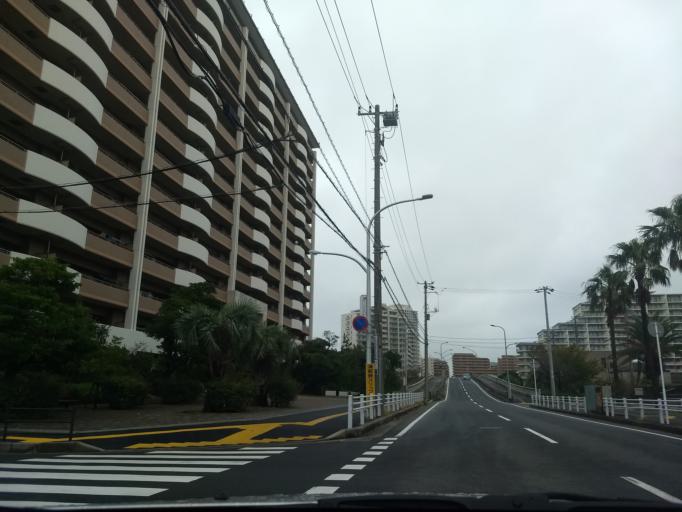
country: JP
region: Tokyo
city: Urayasu
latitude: 35.6362
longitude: 139.9188
